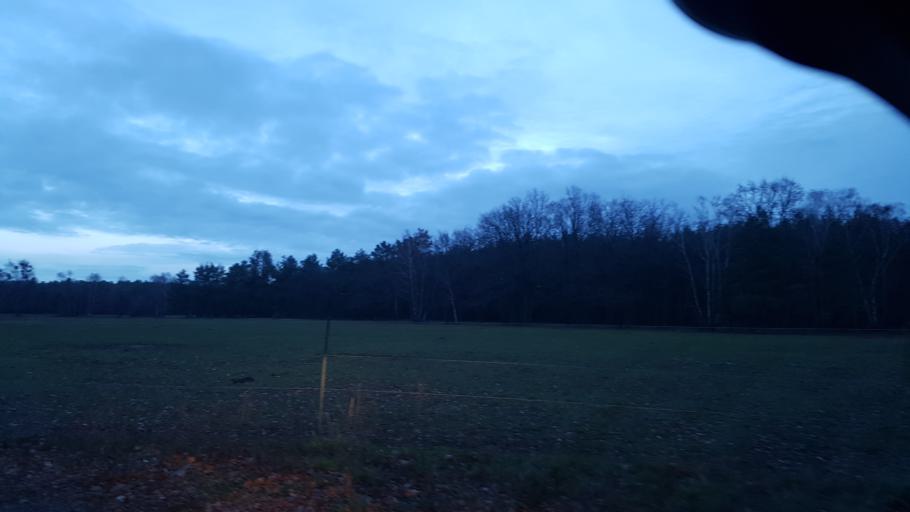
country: DE
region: Berlin
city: Wannsee
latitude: 52.3409
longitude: 13.1440
